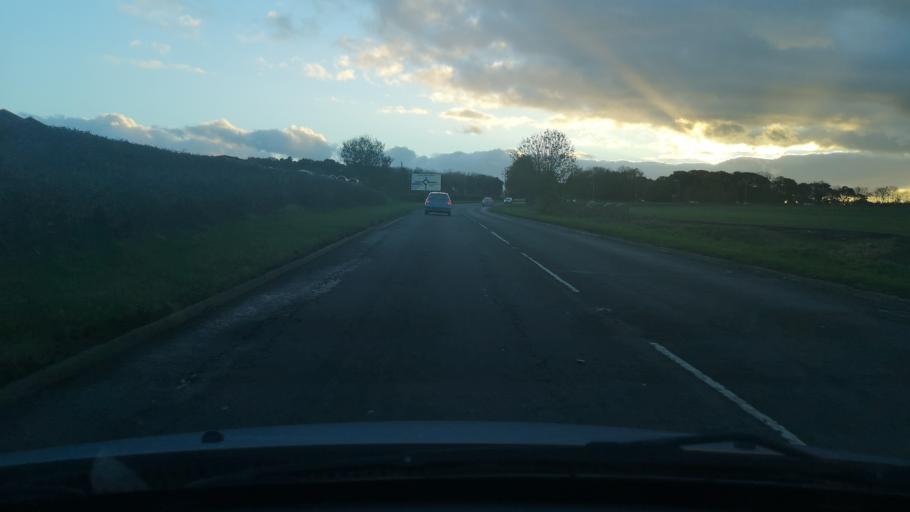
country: GB
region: England
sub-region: City and Borough of Wakefield
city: Middlestown
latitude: 53.6262
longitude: -1.5752
